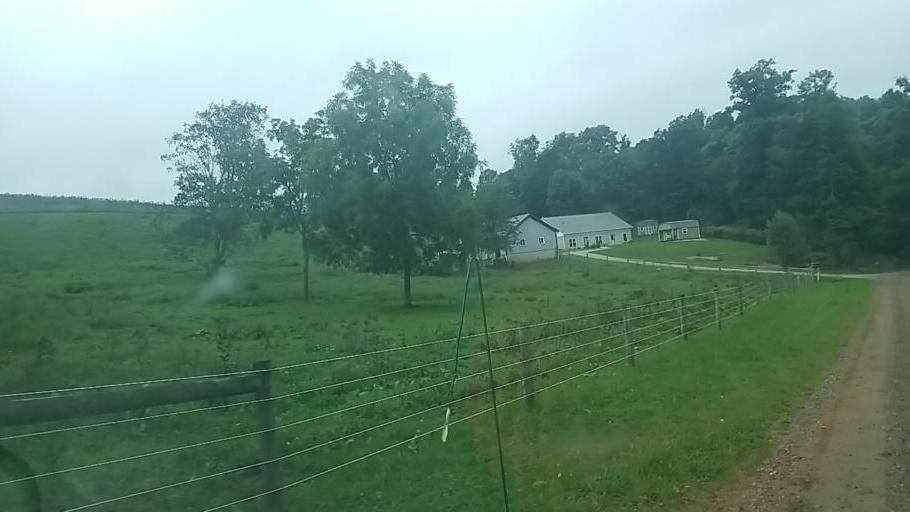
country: US
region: Ohio
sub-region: Knox County
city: Danville
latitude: 40.4935
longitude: -82.1472
